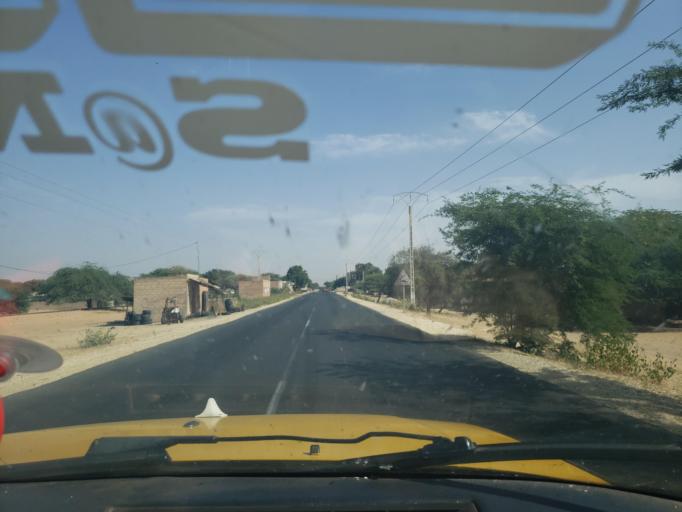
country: SN
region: Saint-Louis
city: Saint-Louis
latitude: 15.9295
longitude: -16.3271
